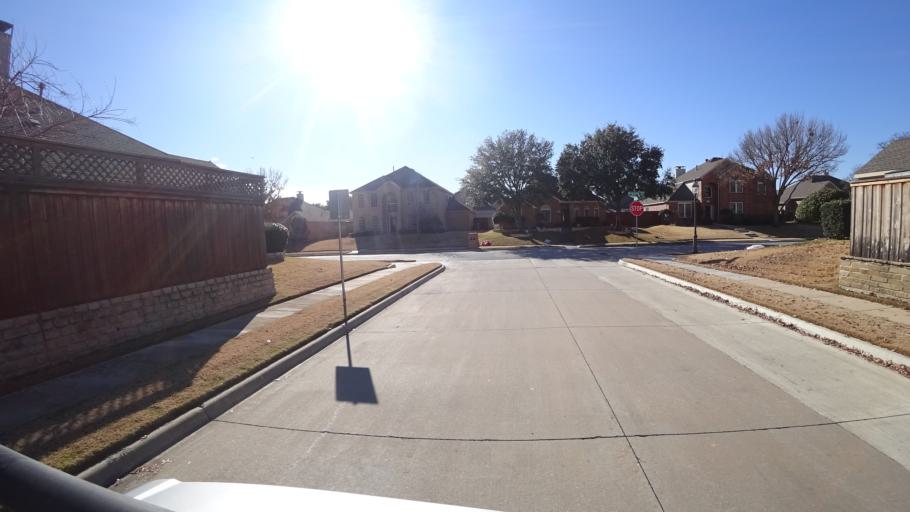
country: US
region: Texas
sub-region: Denton County
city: Lewisville
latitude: 33.0159
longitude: -97.0291
